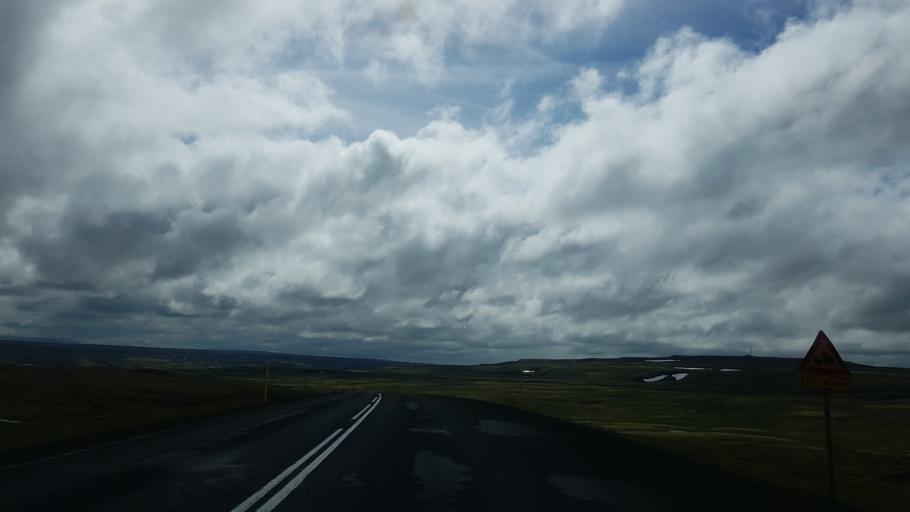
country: IS
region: West
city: Borgarnes
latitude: 64.9773
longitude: -21.0655
